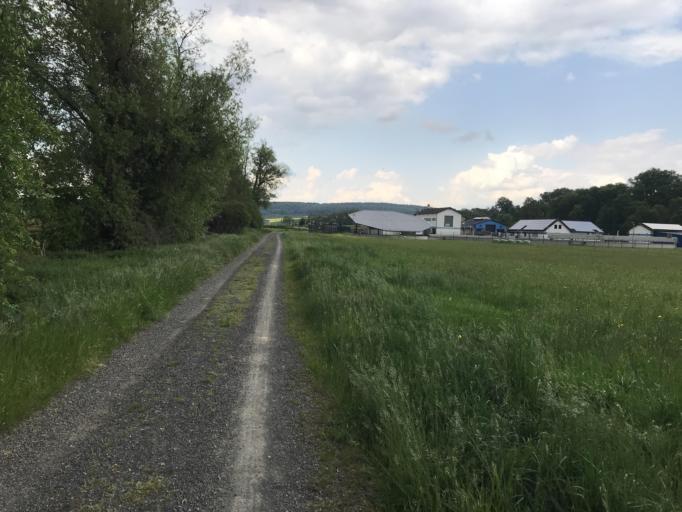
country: DE
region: Hesse
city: Budingen
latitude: 50.2890
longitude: 9.0827
